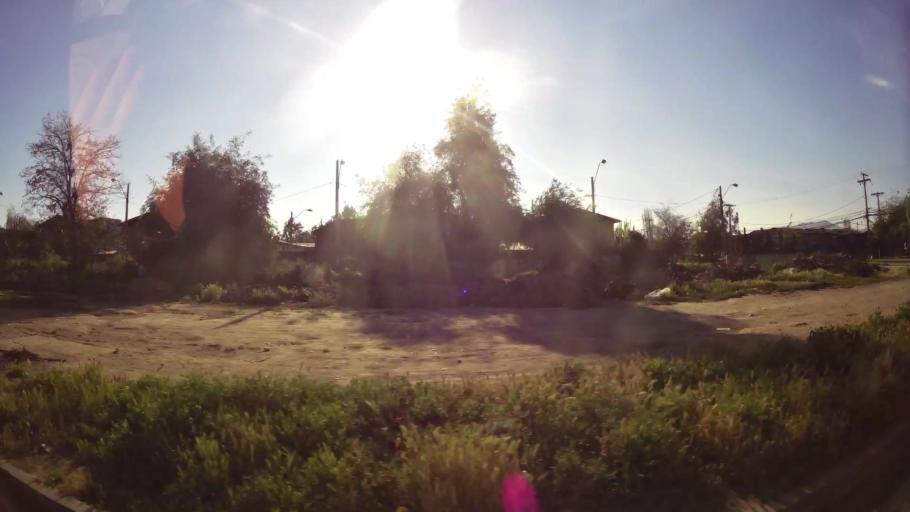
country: CL
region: Santiago Metropolitan
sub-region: Provincia de Talagante
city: Penaflor
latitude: -33.6044
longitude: -70.8665
